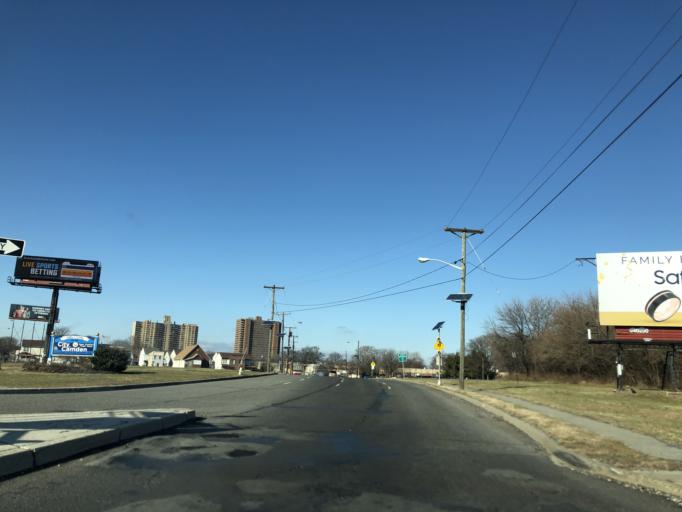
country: US
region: New Jersey
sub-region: Camden County
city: Camden
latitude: 39.9458
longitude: -75.1088
